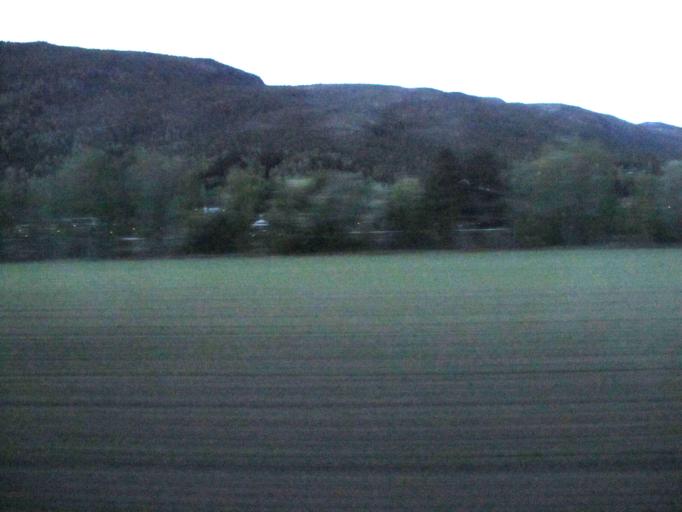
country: NO
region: Oppland
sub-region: Sel
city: Otta
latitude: 61.7336
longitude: 9.5446
